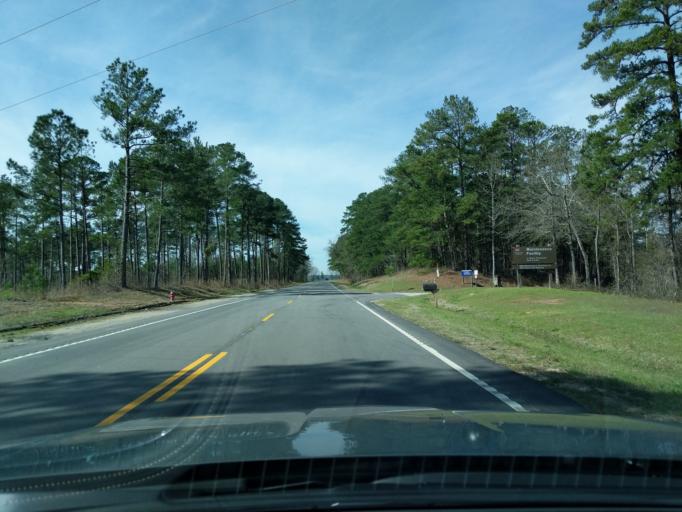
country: US
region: Georgia
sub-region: Columbia County
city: Evans
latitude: 33.6717
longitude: -82.1812
